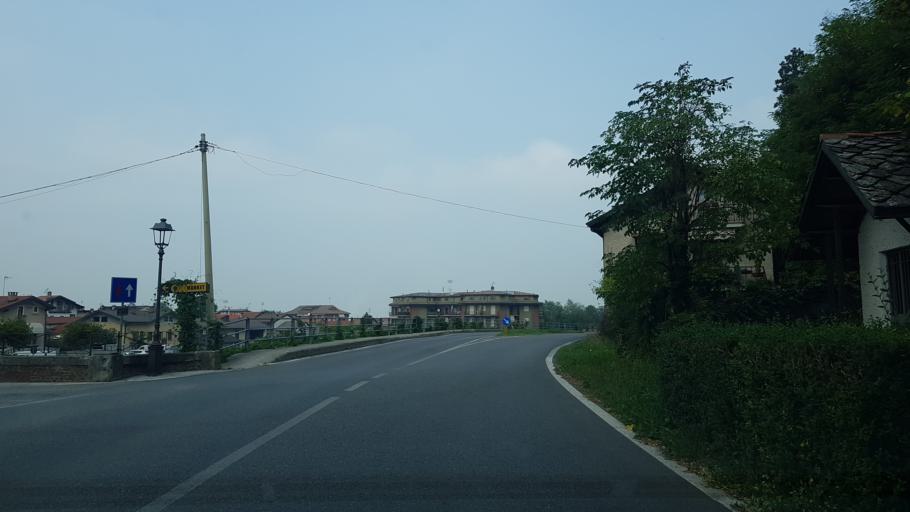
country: IT
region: Piedmont
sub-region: Provincia di Cuneo
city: Chiusa di Pesio
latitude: 44.3248
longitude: 7.6801
